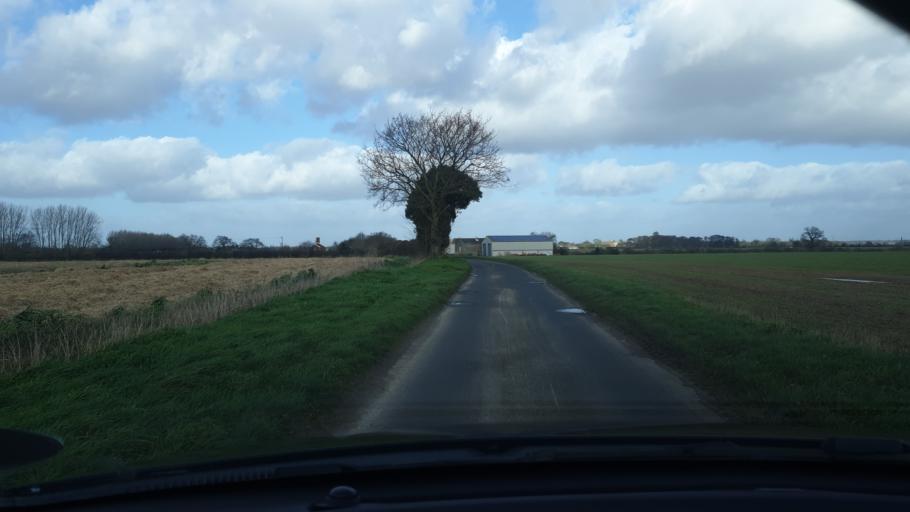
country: GB
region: England
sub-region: Essex
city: Manningtree
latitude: 51.9272
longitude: 1.0604
